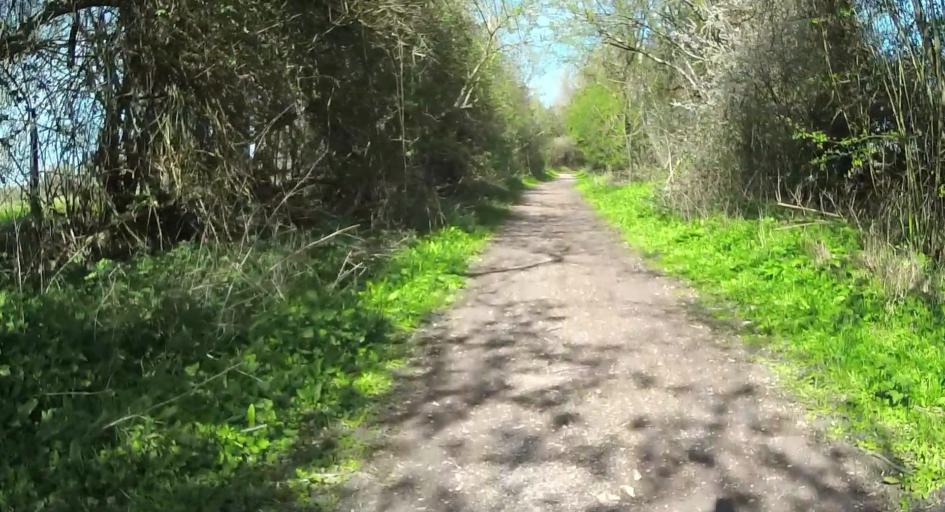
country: GB
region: England
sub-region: Hampshire
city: Romsey
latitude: 51.0690
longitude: -1.5136
